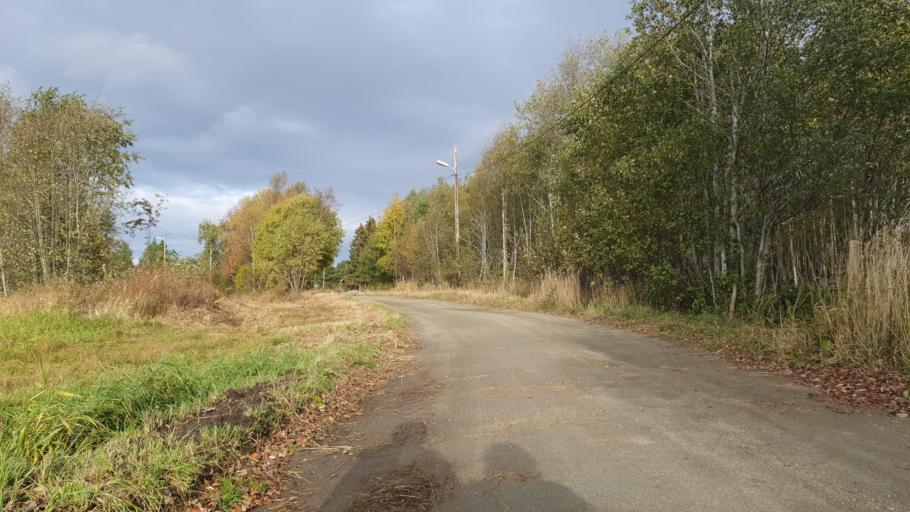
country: NO
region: Sor-Trondelag
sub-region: Klaebu
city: Klaebu
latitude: 63.2946
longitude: 10.4635
